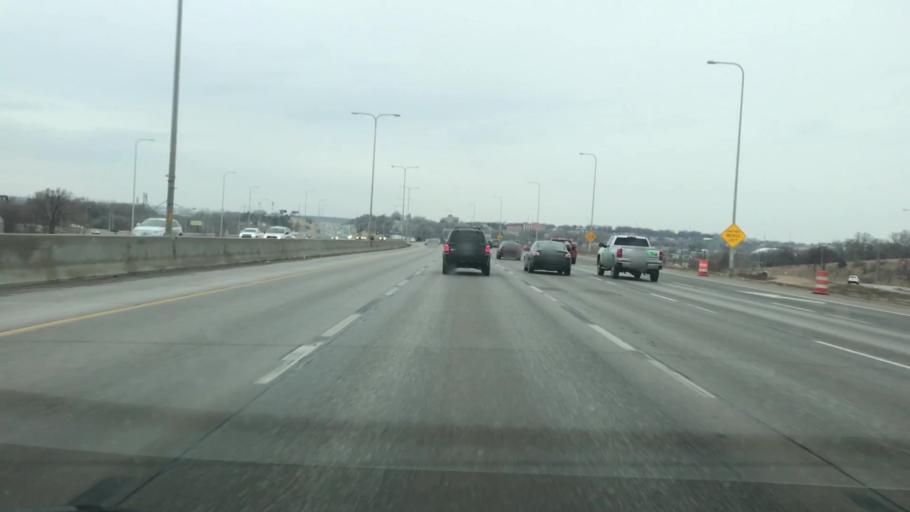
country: US
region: Nebraska
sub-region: Douglas County
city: Ralston
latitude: 41.2237
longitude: -95.9987
